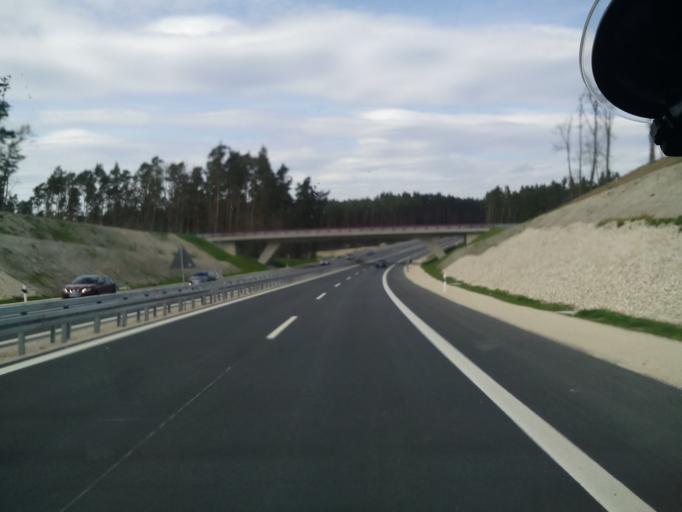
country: DE
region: Bavaria
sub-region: Regierungsbezirk Mittelfranken
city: Roth
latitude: 49.2084
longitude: 11.0745
